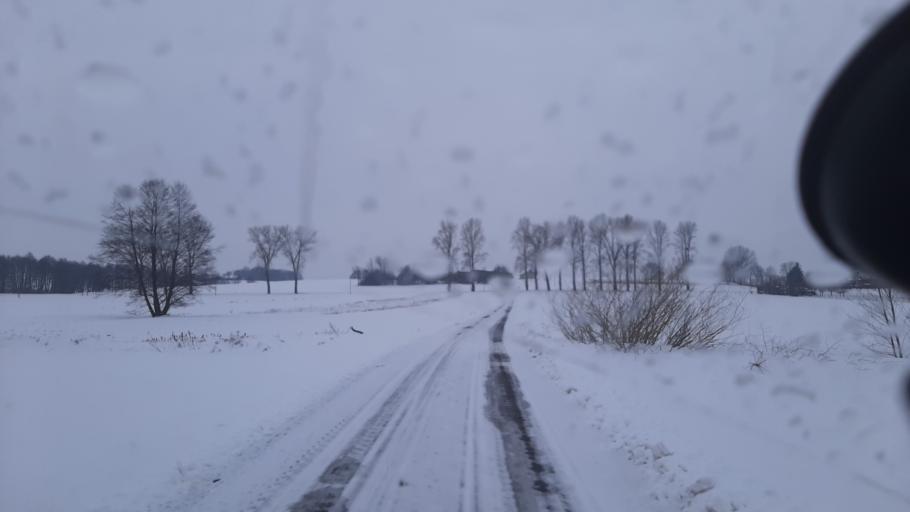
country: PL
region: Lublin Voivodeship
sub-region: Powiat lubelski
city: Jastkow
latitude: 51.3478
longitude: 22.3920
